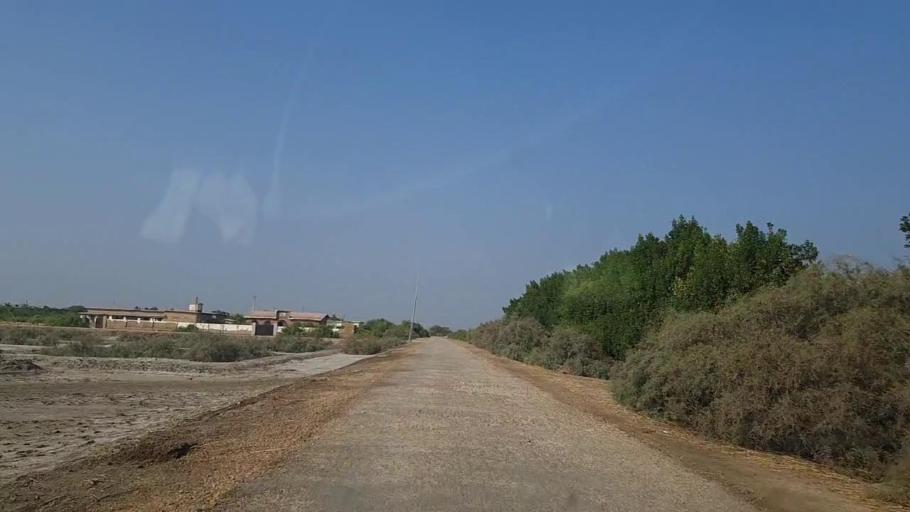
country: PK
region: Sindh
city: Mirpur Sakro
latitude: 24.5678
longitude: 67.6857
